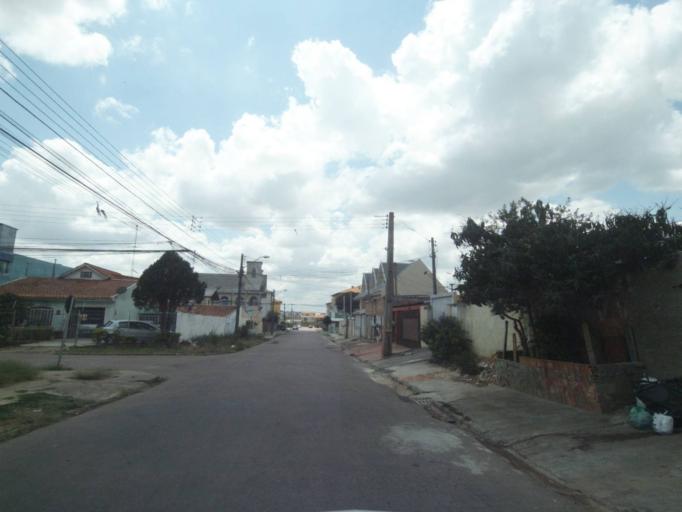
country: BR
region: Parana
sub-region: Sao Jose Dos Pinhais
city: Sao Jose dos Pinhais
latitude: -25.5415
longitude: -49.2680
